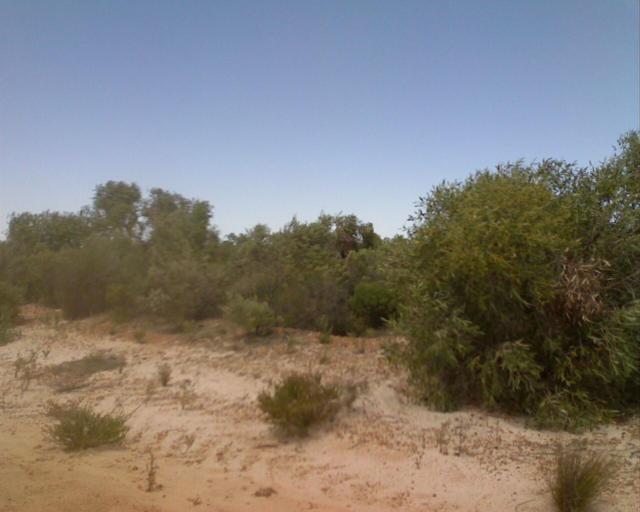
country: AU
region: Western Australia
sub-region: Dandaragan
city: Jurien Bay
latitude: -30.0729
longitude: 115.6250
